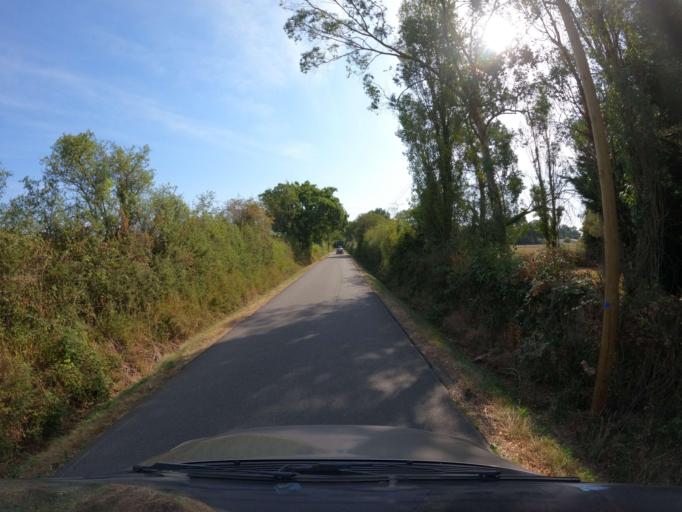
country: FR
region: Pays de la Loire
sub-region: Departement de la Vendee
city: Challans
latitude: 46.8091
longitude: -1.8408
